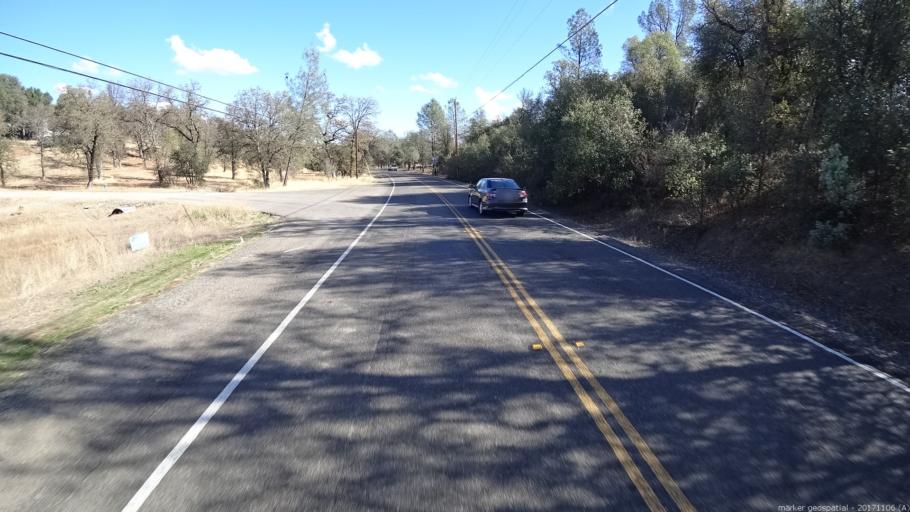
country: US
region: California
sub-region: Shasta County
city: Palo Cedro
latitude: 40.5912
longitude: -122.2785
